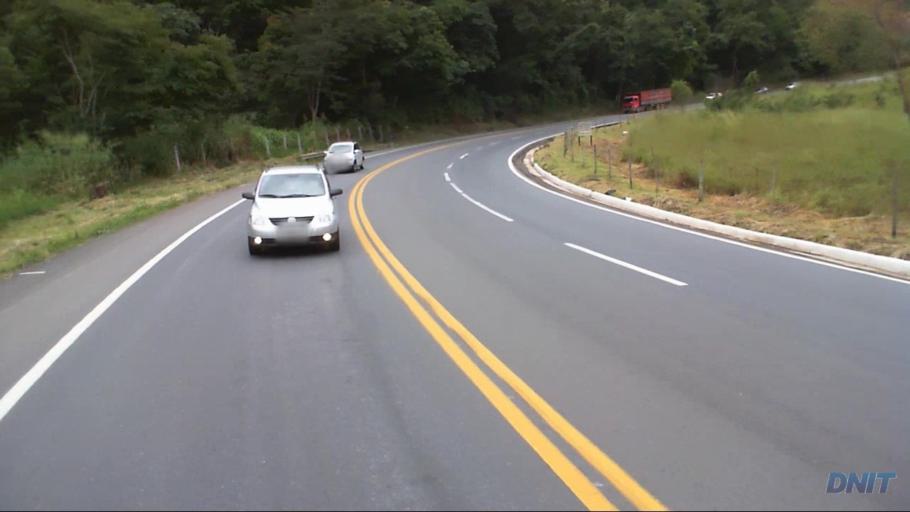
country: BR
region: Minas Gerais
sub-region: Joao Monlevade
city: Joao Monlevade
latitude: -19.8548
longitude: -43.2271
